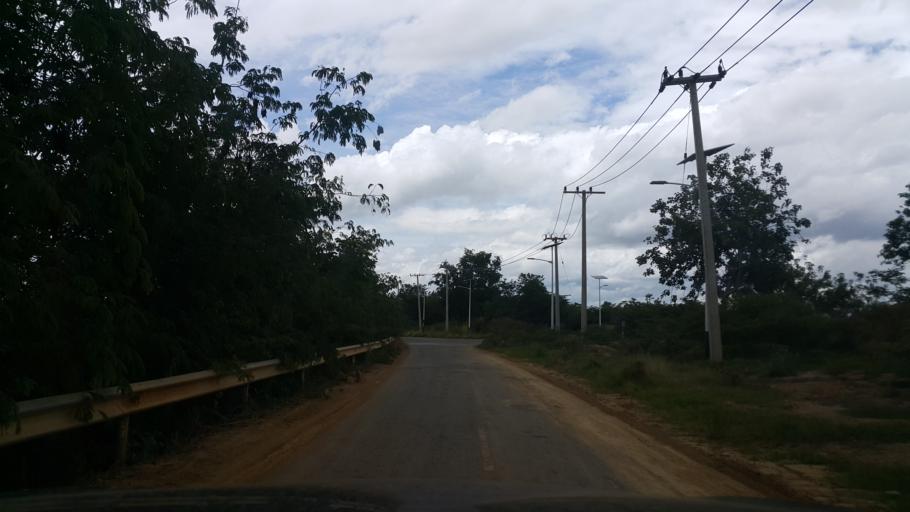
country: TH
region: Sukhothai
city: Ban Na
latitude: 17.0594
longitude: 99.7759
